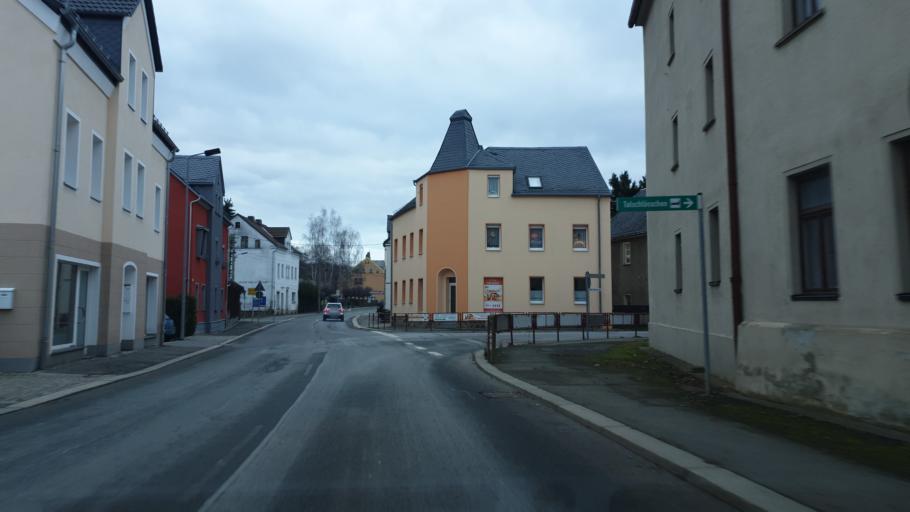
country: DE
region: Saxony
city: Bernsdorf
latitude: 50.7444
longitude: 12.6571
